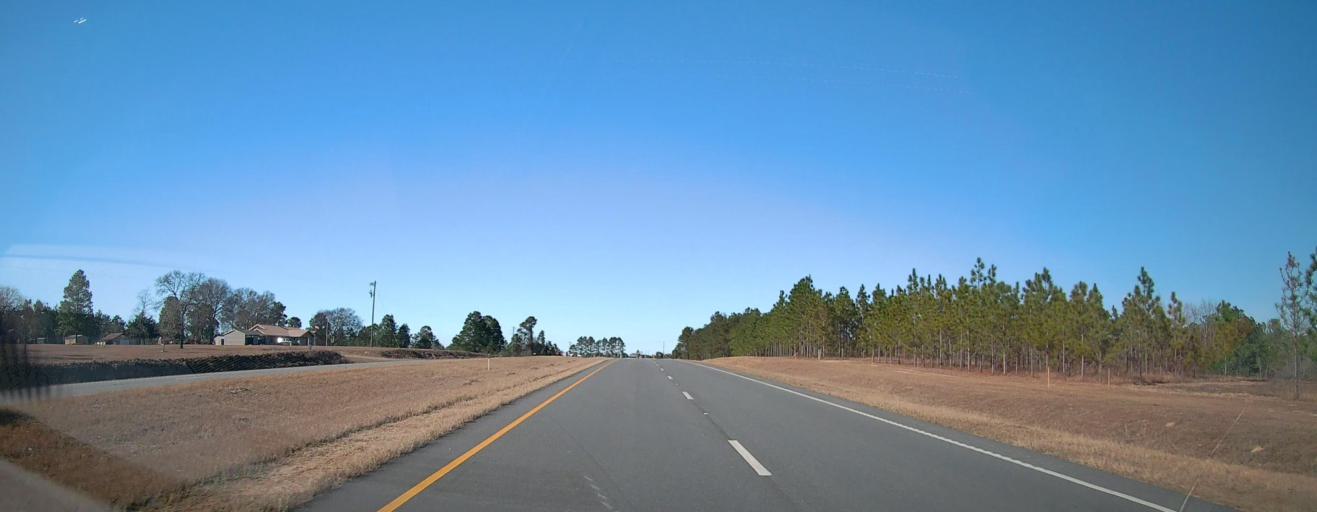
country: US
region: Georgia
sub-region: Taylor County
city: Butler
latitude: 32.5915
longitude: -84.2371
